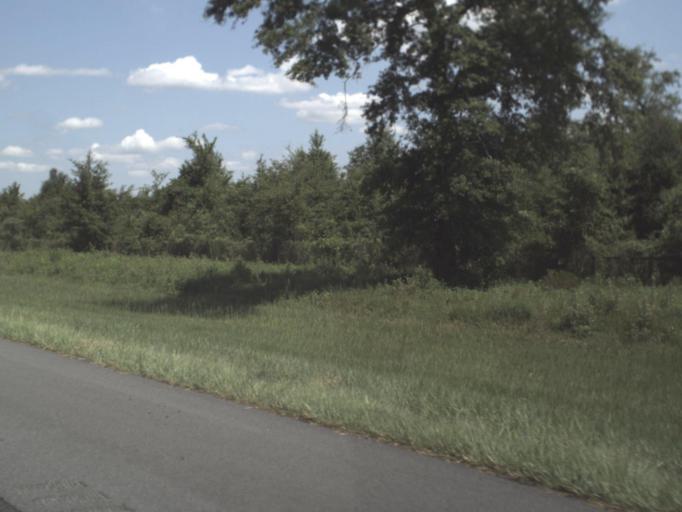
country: US
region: Florida
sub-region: Madison County
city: Madison
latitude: 30.3837
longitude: -83.3112
